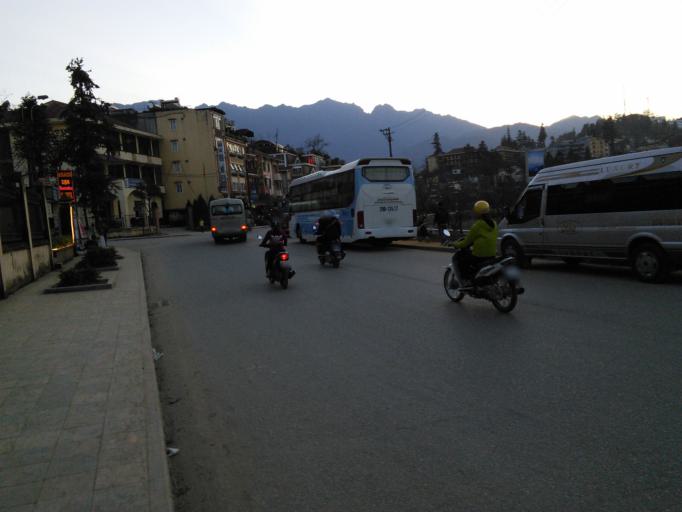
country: VN
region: Lao Cai
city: Sa Pa
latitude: 22.3375
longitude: 103.8468
